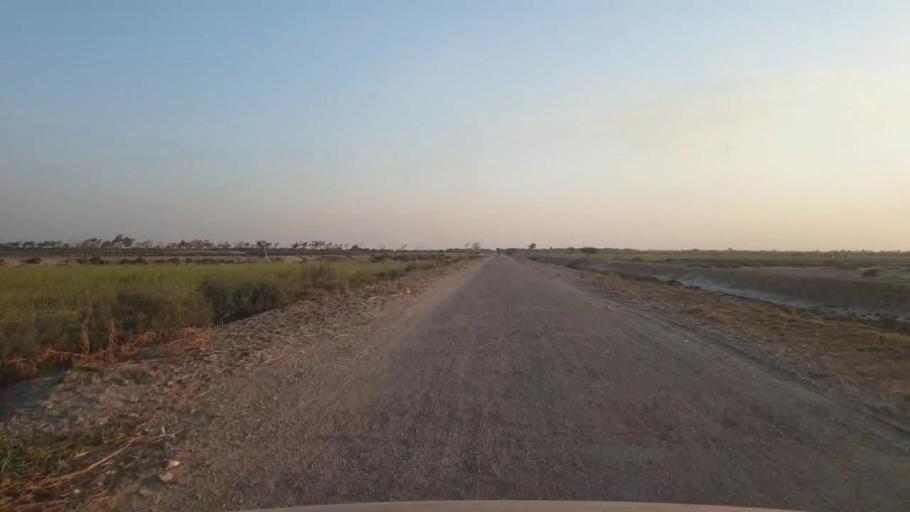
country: PK
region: Sindh
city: Mirwah Gorchani
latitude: 25.2765
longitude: 68.9394
